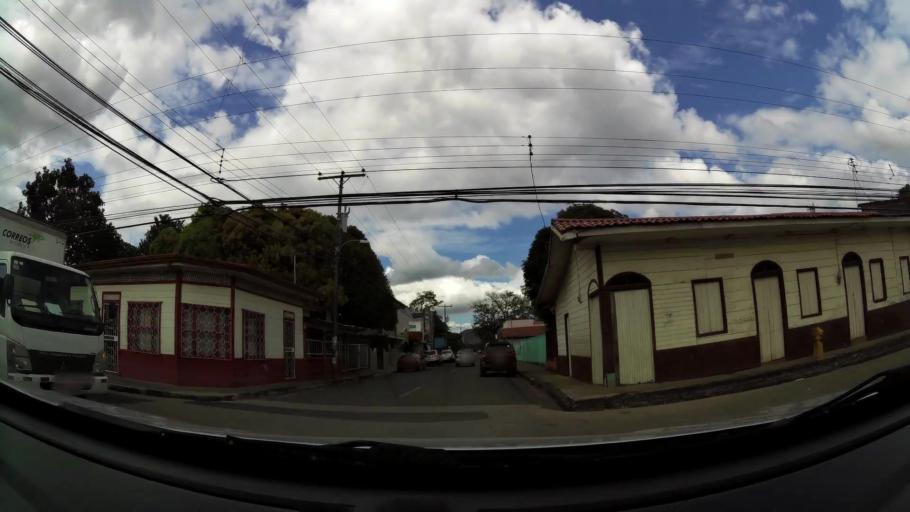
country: CR
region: Guanacaste
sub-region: Canton de Nicoya
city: Nicoya
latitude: 10.1431
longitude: -85.4542
